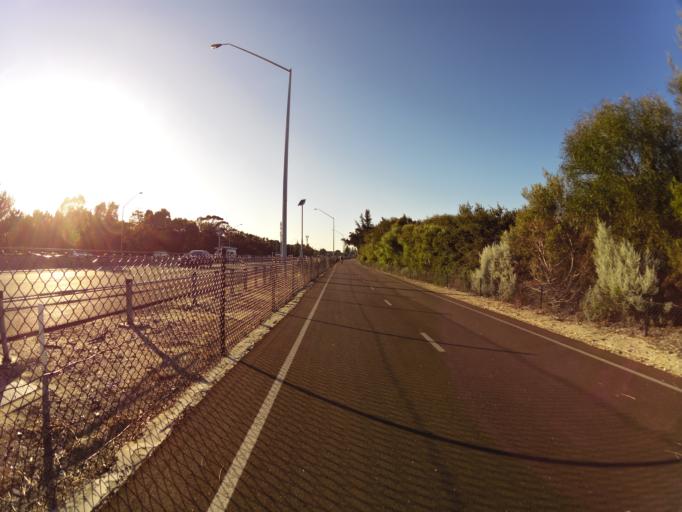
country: AU
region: Western Australia
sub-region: South Perth
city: Como
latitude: -31.9839
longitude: 115.8510
